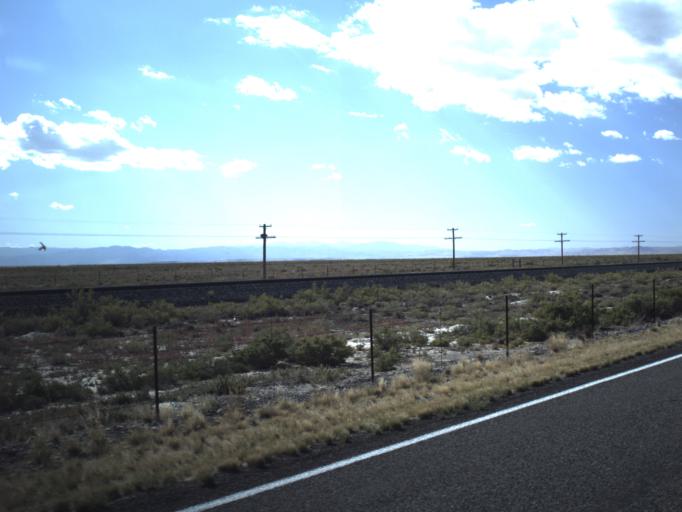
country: US
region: Utah
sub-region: Millard County
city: Delta
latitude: 39.0956
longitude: -112.7494
